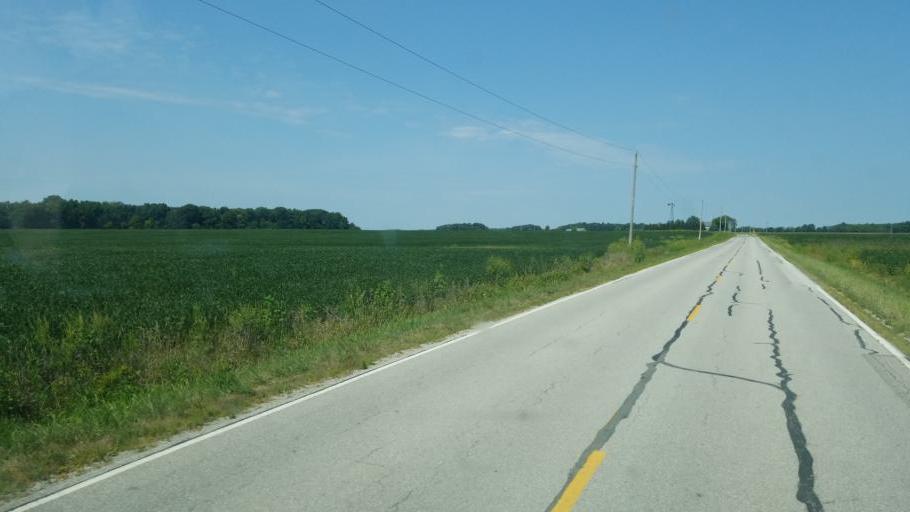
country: US
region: Ohio
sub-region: Marion County
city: Marion
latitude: 40.6823
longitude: -83.2363
